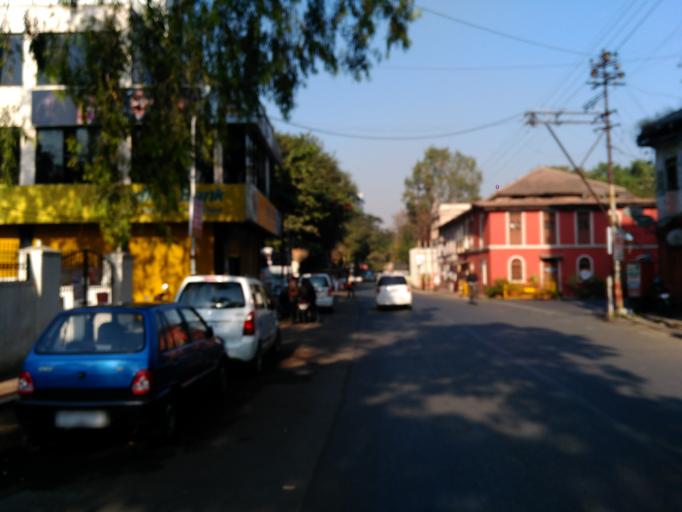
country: IN
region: Maharashtra
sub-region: Pune Division
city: Pune
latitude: 18.5154
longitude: 73.8759
